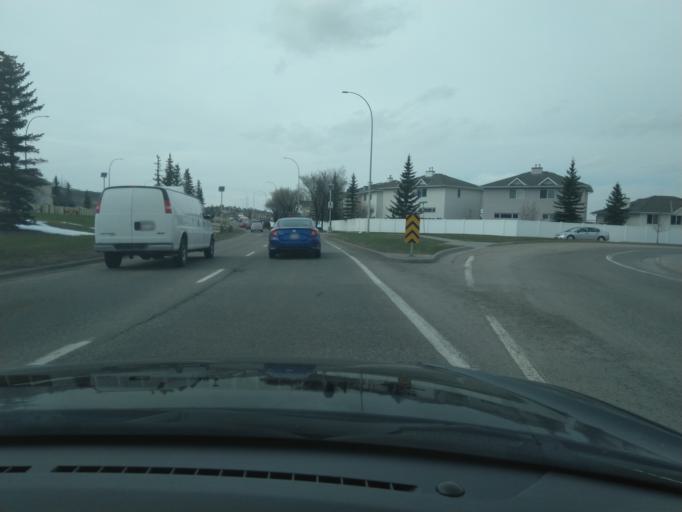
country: CA
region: Alberta
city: Calgary
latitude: 51.1514
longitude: -114.0640
